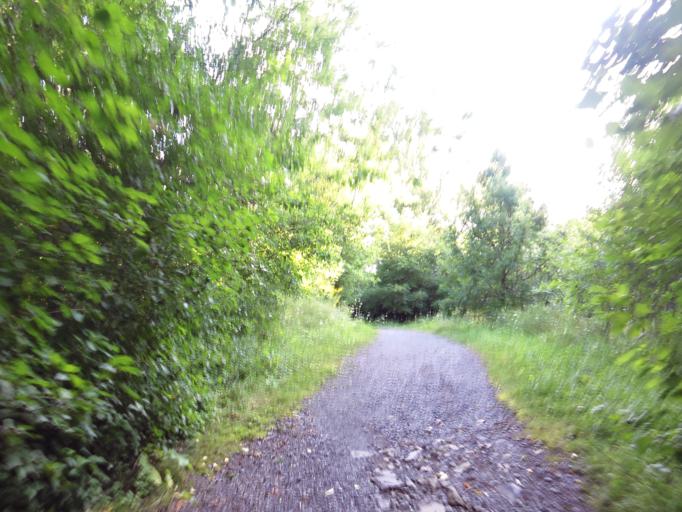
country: CA
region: Ontario
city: Ottawa
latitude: 45.3667
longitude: -75.6972
